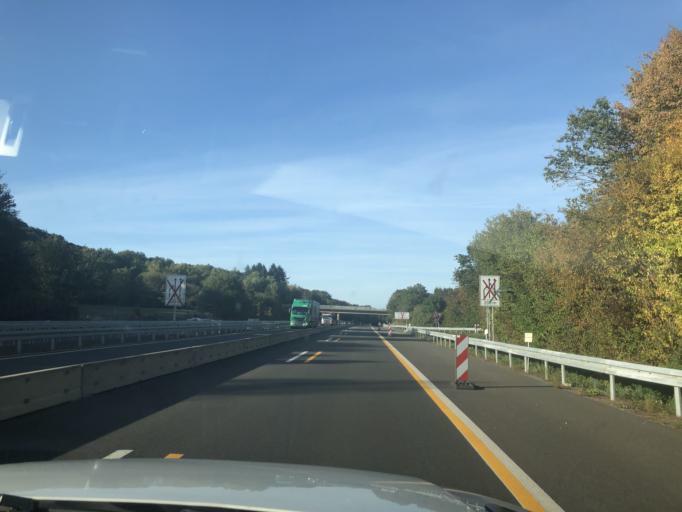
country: DE
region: Saarland
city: Tholey
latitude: 49.5054
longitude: 6.9928
